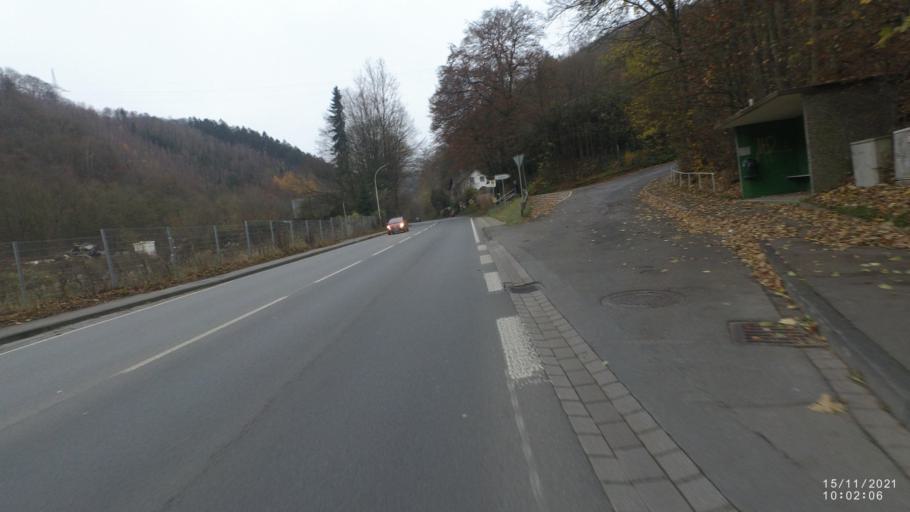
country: DE
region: North Rhine-Westphalia
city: Werdohl
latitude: 51.2450
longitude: 7.7608
